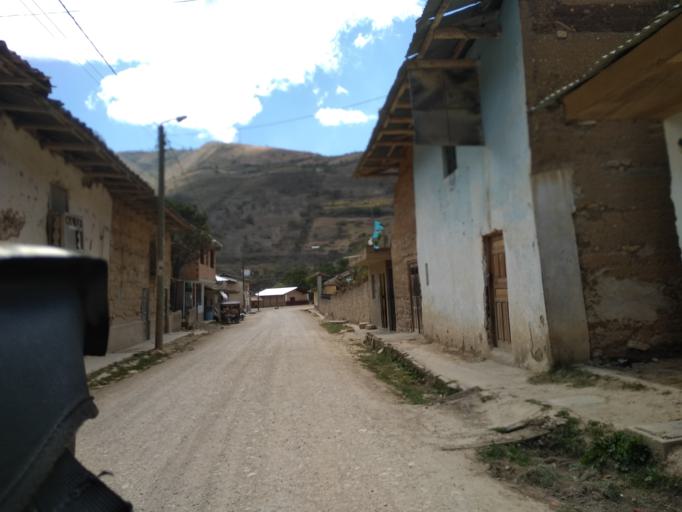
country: PE
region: Amazonas
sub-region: Provincia de Chachapoyas
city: Duraznopampa
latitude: -6.5594
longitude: -77.8308
